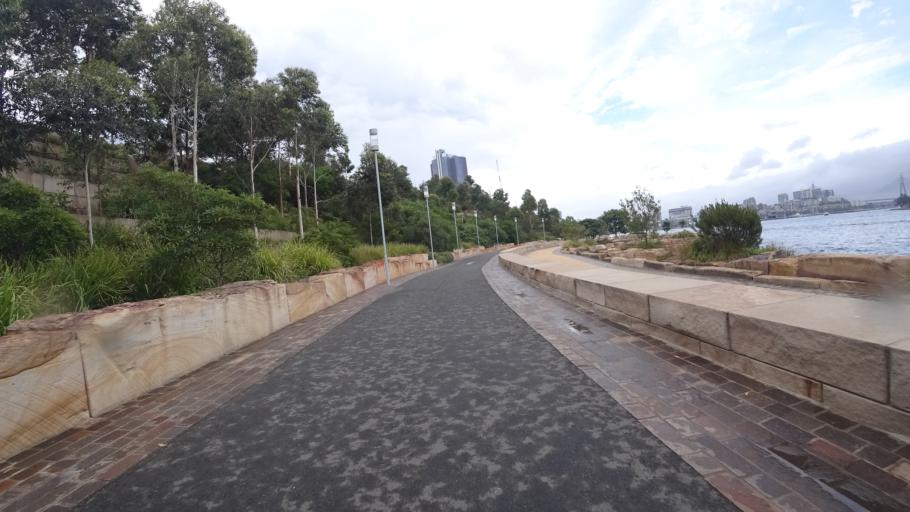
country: AU
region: New South Wales
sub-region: Leichhardt
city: Balmain East
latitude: -33.8567
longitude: 151.2005
